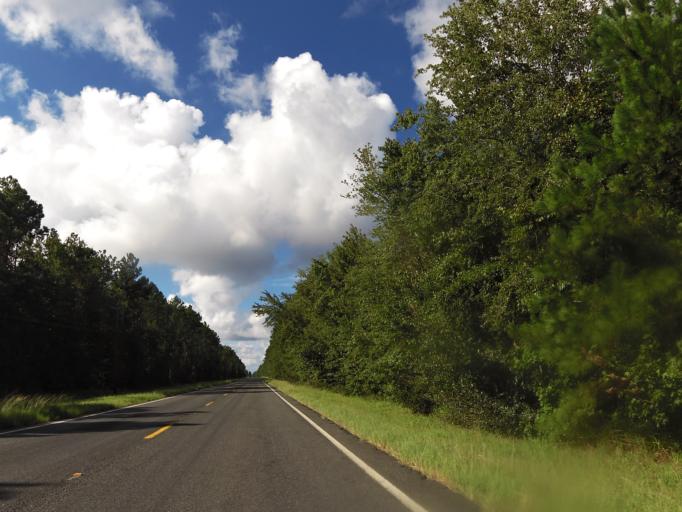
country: US
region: Georgia
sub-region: Camden County
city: Woodbine
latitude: 30.8993
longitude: -81.7098
